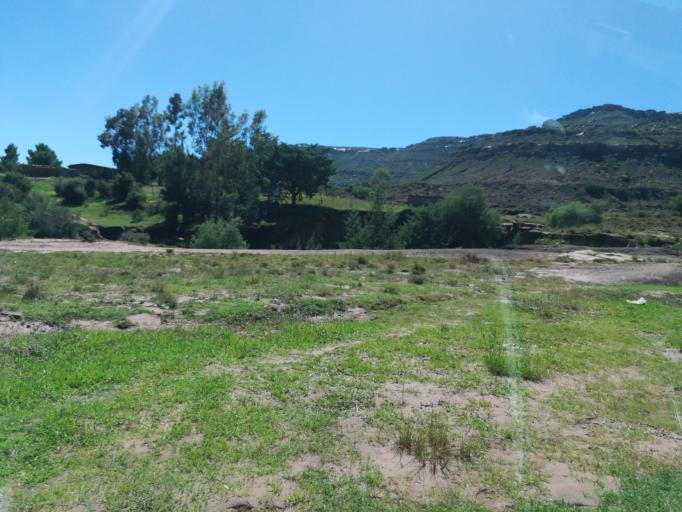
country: LS
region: Quthing
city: Quthing
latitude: -30.3382
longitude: 27.5348
